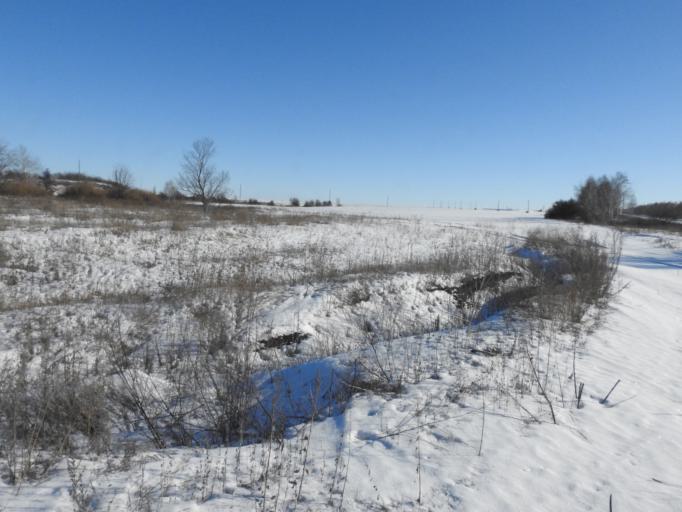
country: RU
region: Saratov
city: Lysyye Gory
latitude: 51.4574
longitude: 44.9162
